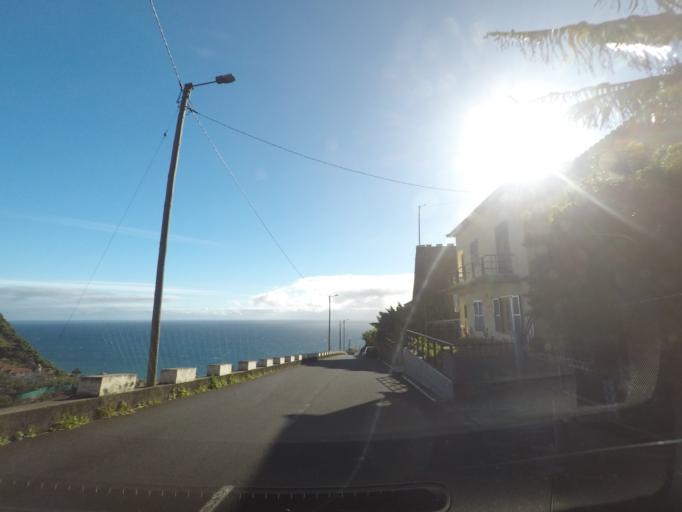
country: PT
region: Madeira
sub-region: Calheta
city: Arco da Calheta
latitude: 32.7065
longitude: -17.1346
